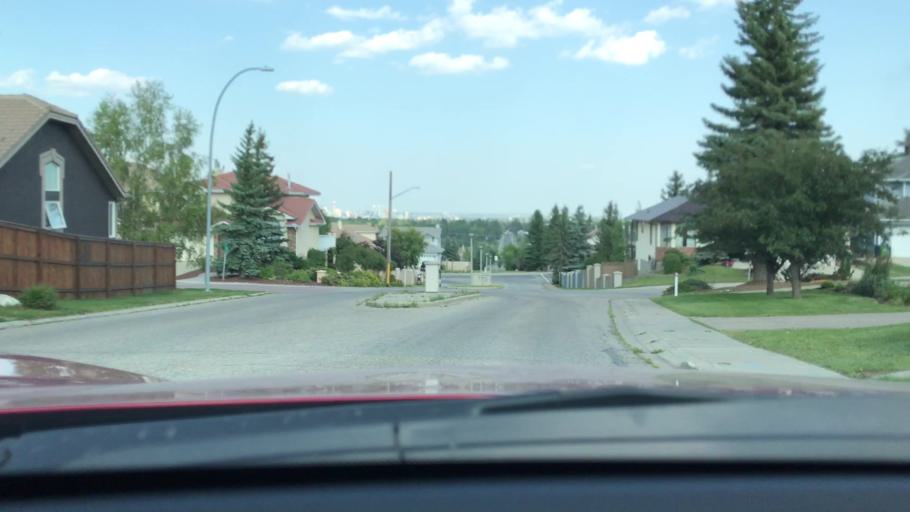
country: CA
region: Alberta
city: Calgary
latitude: 51.0305
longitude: -114.1726
